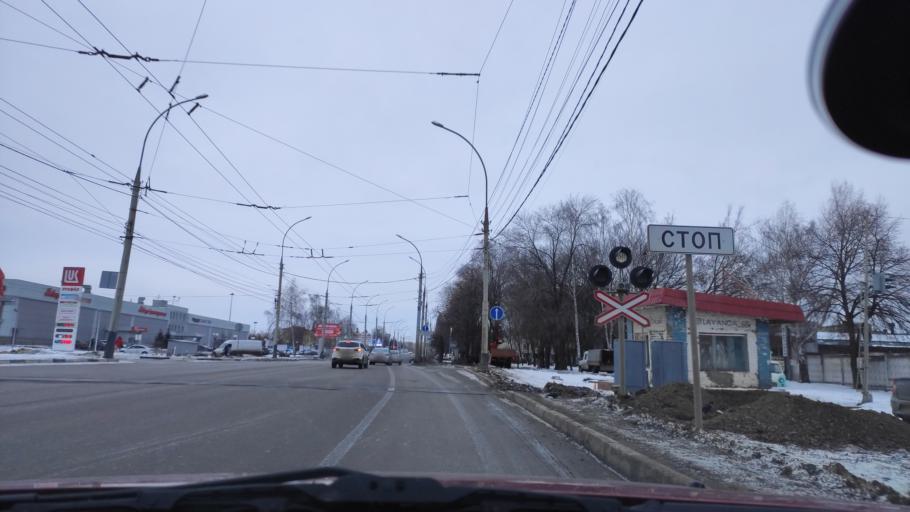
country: RU
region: Tambov
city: Tambov
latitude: 52.7510
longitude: 41.4487
